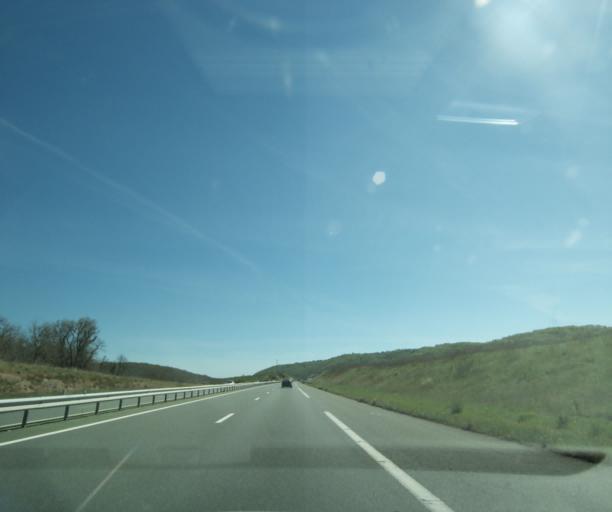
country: FR
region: Midi-Pyrenees
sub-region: Departement du Lot
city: Souillac
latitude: 44.8151
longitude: 1.5011
